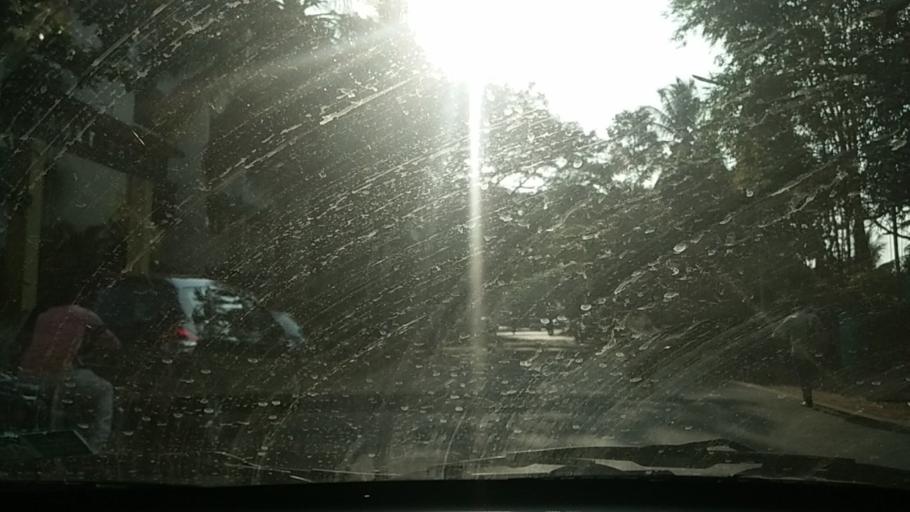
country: IN
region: Goa
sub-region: North Goa
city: Panaji
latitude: 15.4832
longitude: 73.8155
